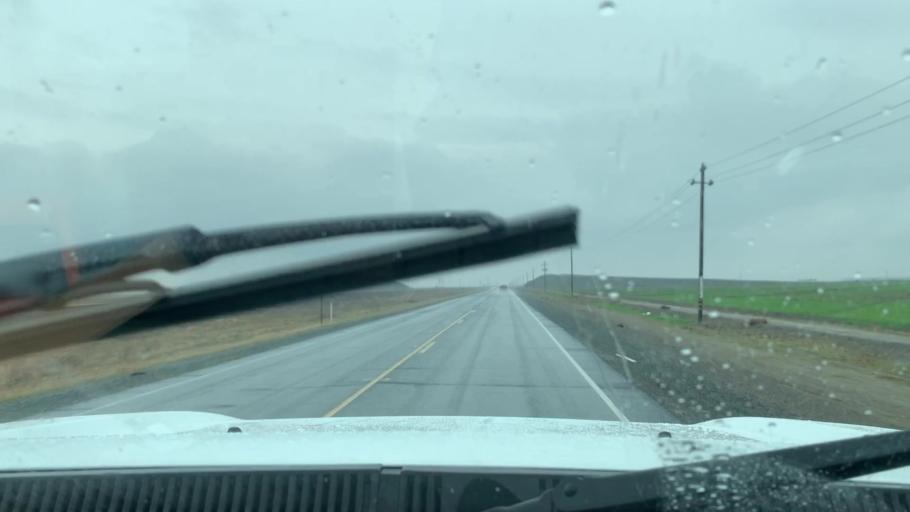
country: US
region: California
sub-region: Tulare County
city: Alpaugh
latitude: 35.9425
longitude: -119.4425
